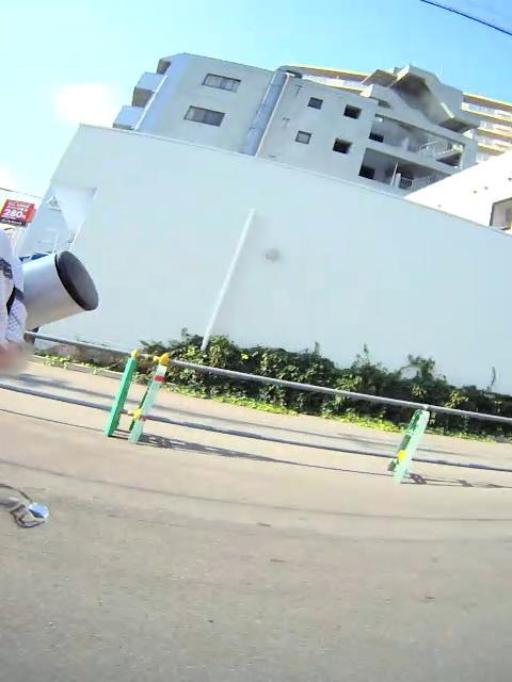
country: JP
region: Osaka
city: Suita
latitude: 34.7378
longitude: 135.5171
